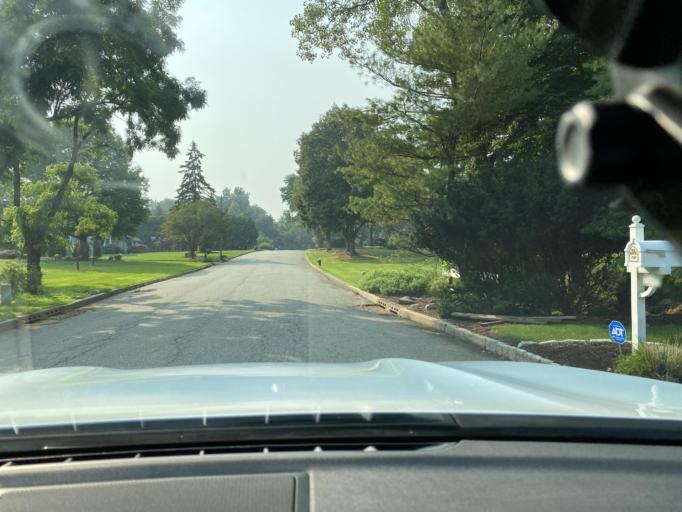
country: US
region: New York
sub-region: Rockland County
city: Airmont
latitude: 41.0931
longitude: -74.1193
